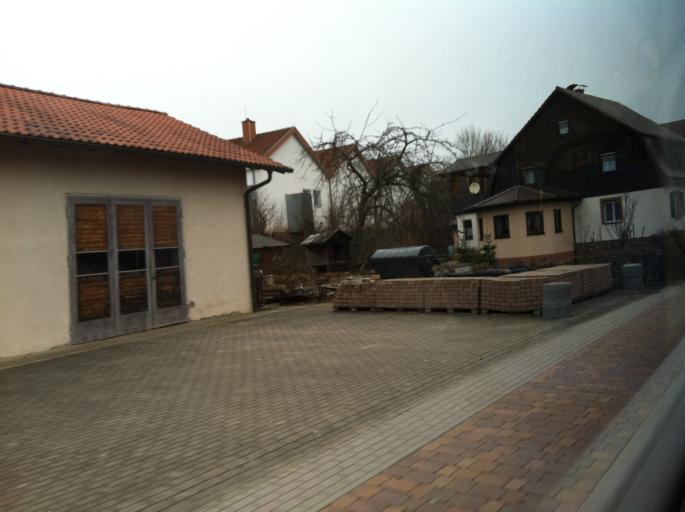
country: DE
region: Baden-Wuerttemberg
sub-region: Karlsruhe Region
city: Mudau
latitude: 49.5298
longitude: 9.2046
